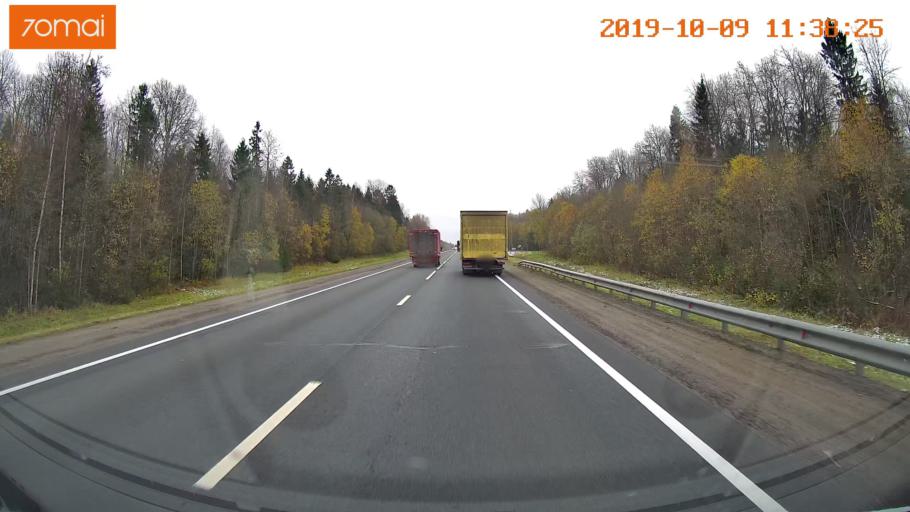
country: RU
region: Vologda
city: Gryazovets
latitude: 58.9685
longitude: 40.1555
